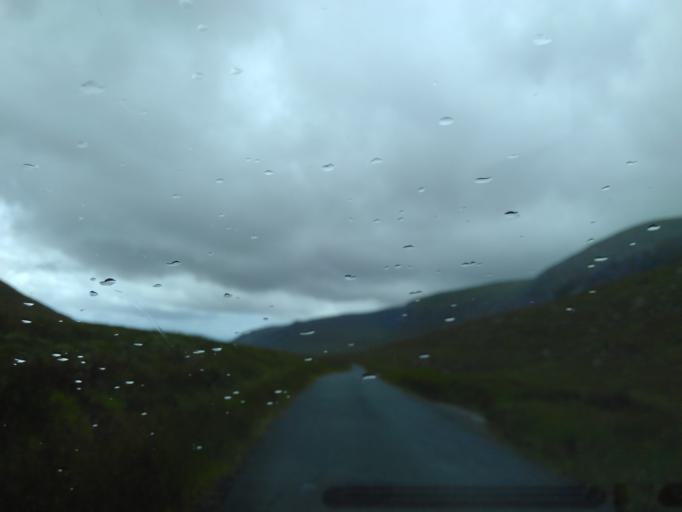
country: IE
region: Ulster
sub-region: County Donegal
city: Dunlewy
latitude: 54.9765
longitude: -8.0731
